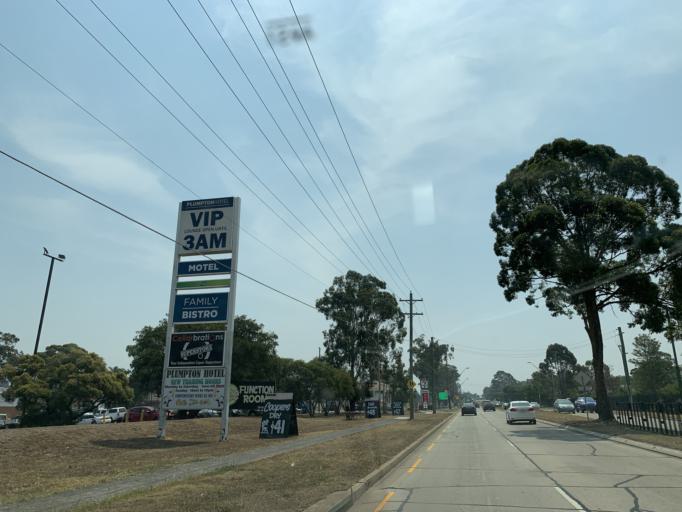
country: AU
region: New South Wales
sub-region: Blacktown
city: Glendenning
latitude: -33.7400
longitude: 150.8615
